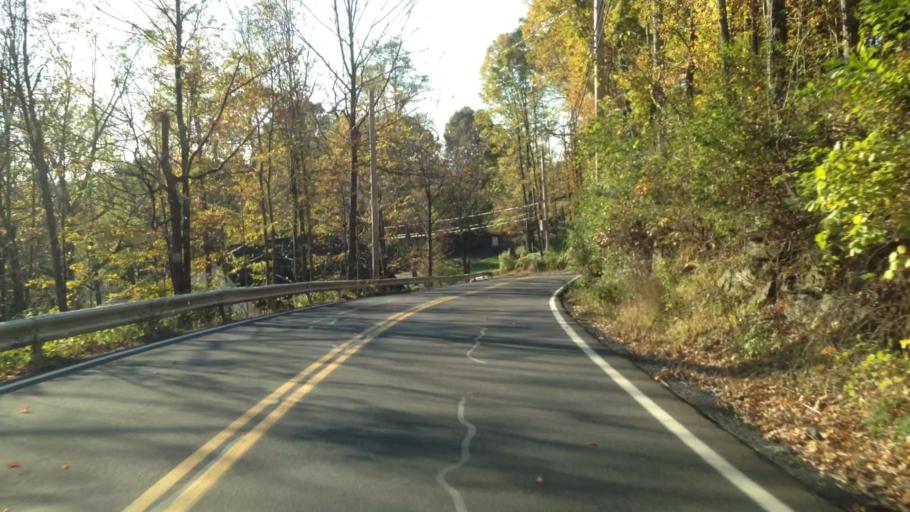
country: US
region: New York
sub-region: Dutchess County
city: Hyde Park
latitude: 41.8263
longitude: -73.9878
